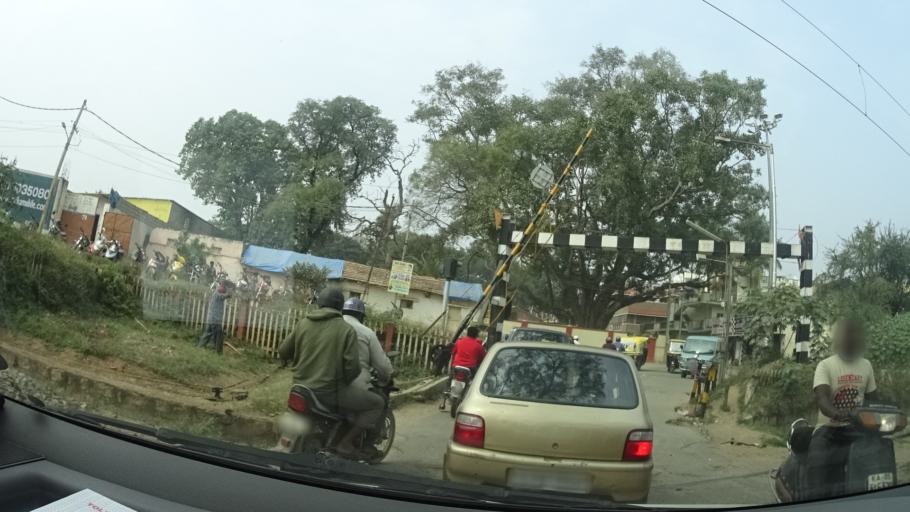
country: IN
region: Karnataka
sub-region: Bangalore Urban
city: Bangalore
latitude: 13.0211
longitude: 77.6234
